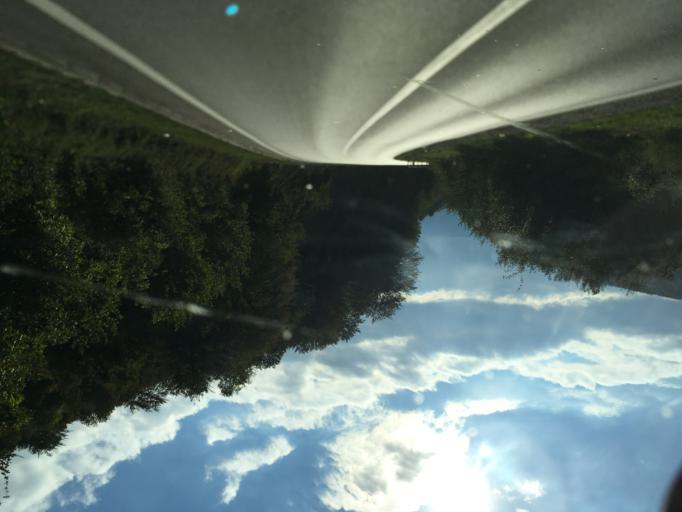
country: BA
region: Federation of Bosnia and Herzegovina
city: Bugojno
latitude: 44.0828
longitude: 17.5207
